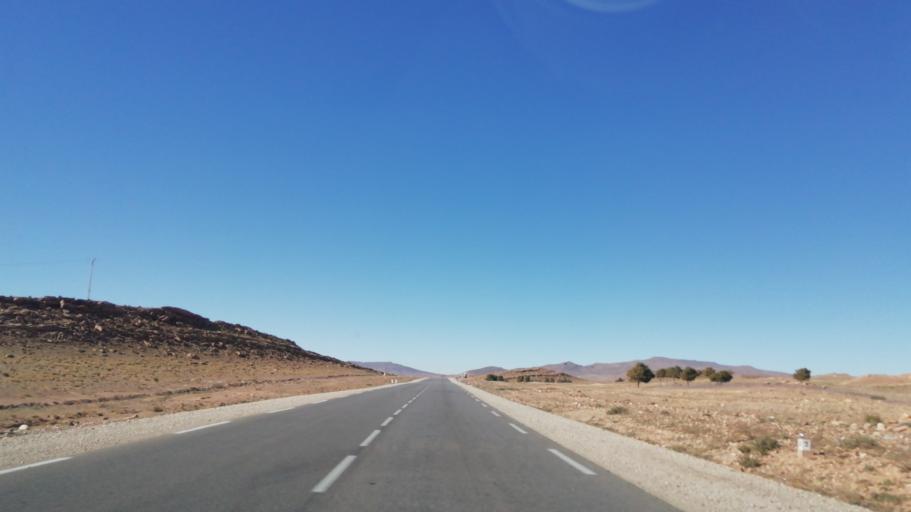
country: DZ
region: El Bayadh
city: El Bayadh
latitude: 33.6099
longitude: 1.2350
